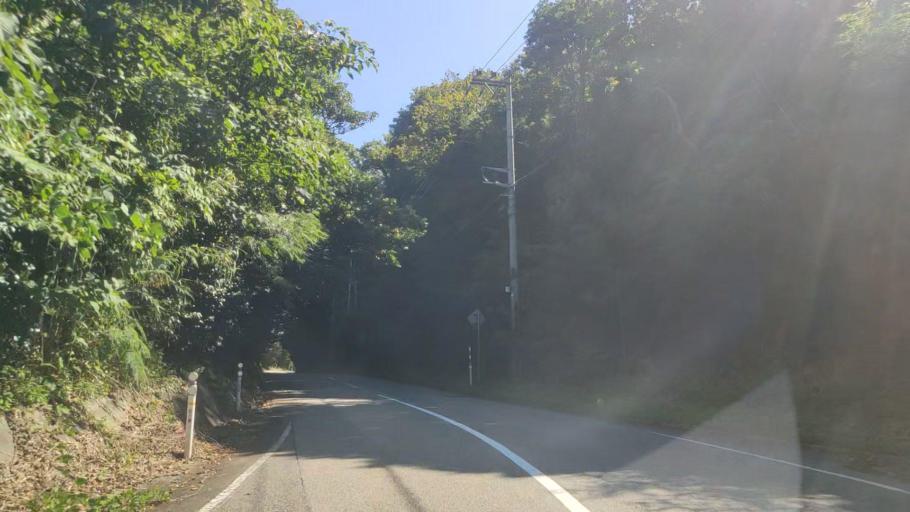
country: JP
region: Ishikawa
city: Nanao
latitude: 37.5211
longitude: 137.3263
